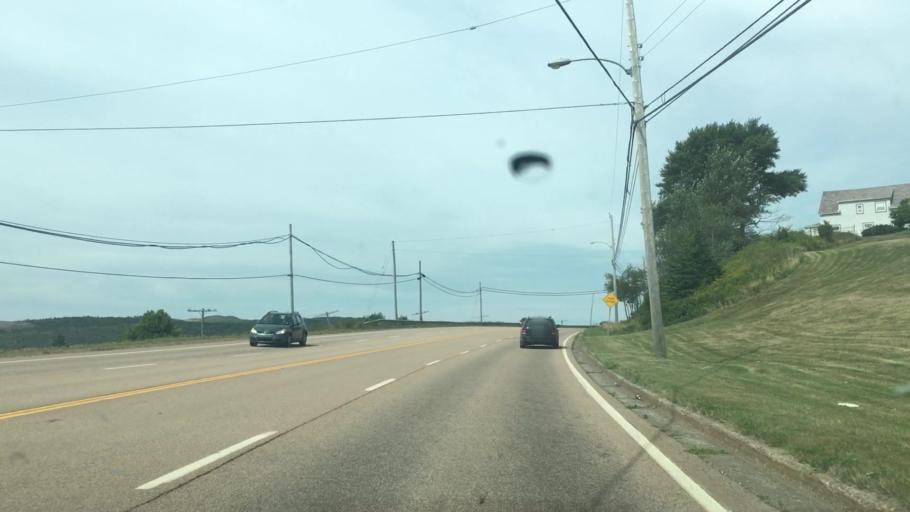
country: CA
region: Nova Scotia
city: Port Hawkesbury
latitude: 45.6259
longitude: -61.3705
